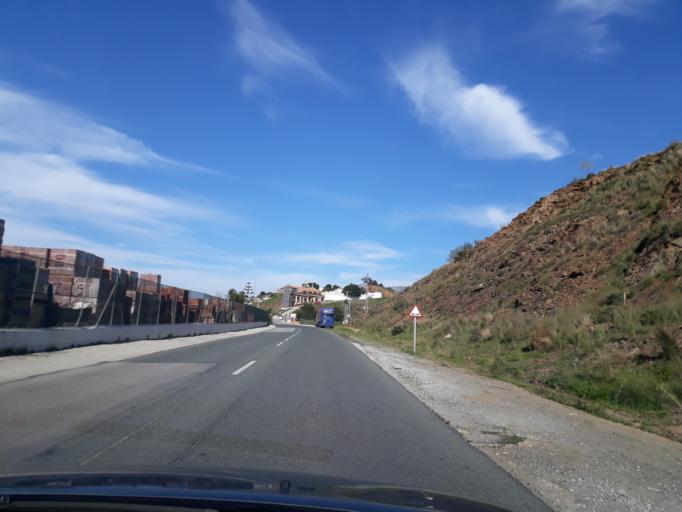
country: ES
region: Andalusia
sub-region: Provincia de Malaga
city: Fuengirola
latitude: 36.5189
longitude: -4.6844
